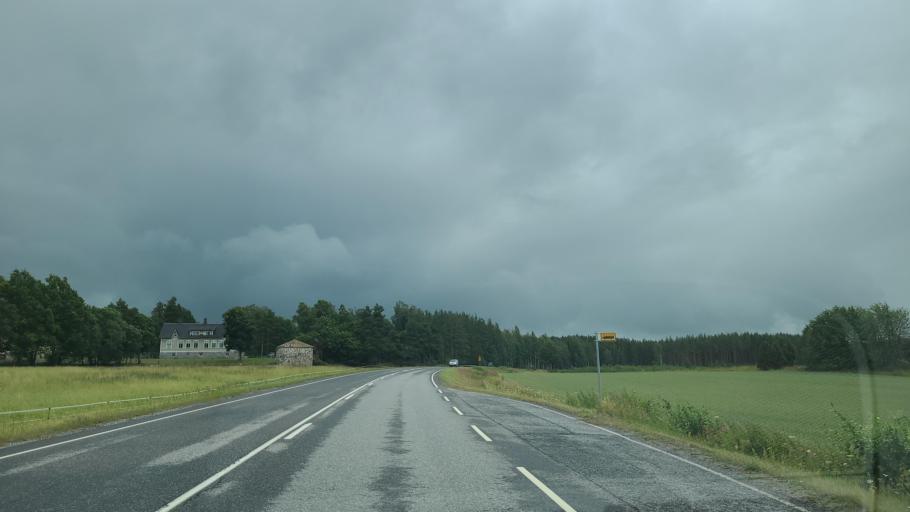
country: FI
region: Varsinais-Suomi
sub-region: Turku
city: Sauvo
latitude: 60.3303
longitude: 22.7131
